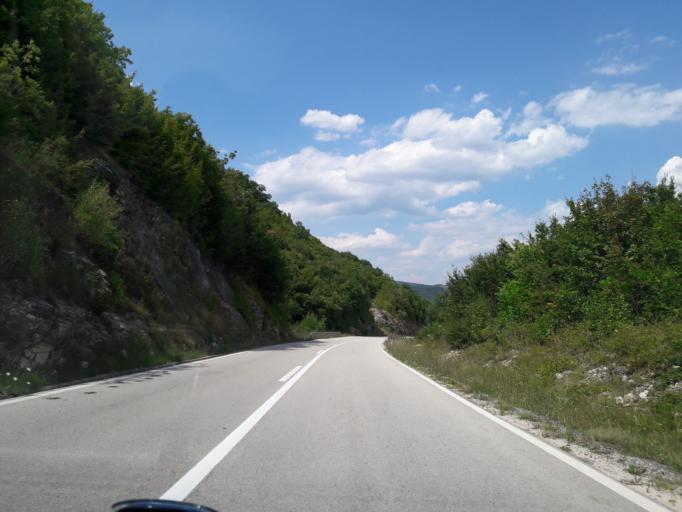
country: BA
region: Republika Srpska
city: Mrkonjic Grad
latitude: 44.5209
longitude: 17.1509
